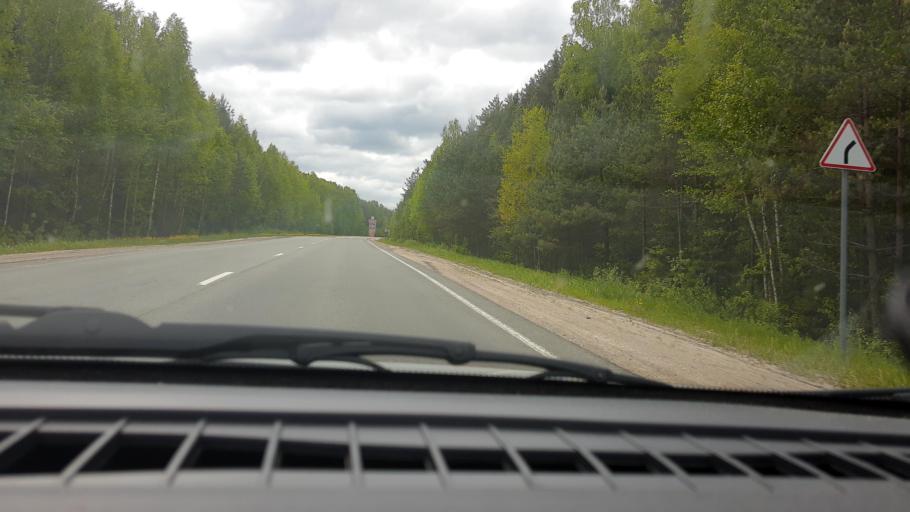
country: RU
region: Nizjnij Novgorod
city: Semenov
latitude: 56.7690
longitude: 44.4134
